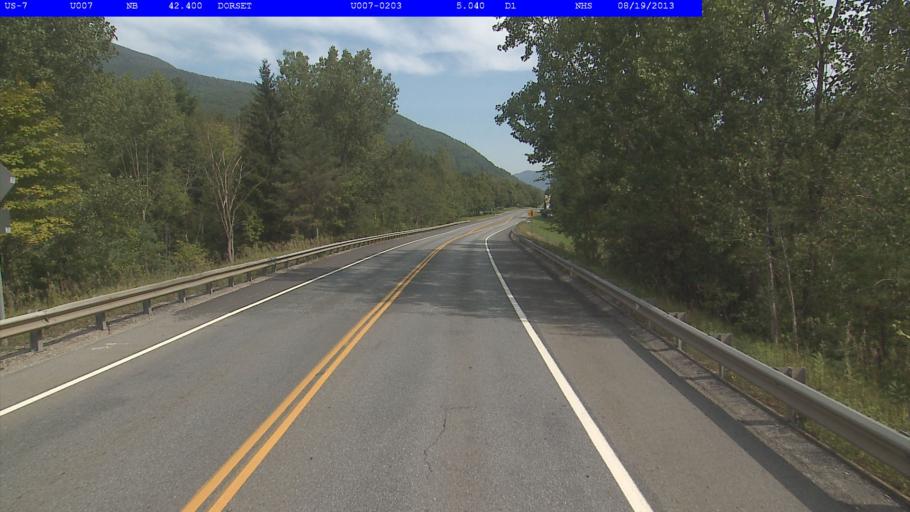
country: US
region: Vermont
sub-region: Bennington County
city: Manchester Center
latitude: 43.2813
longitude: -73.0030
